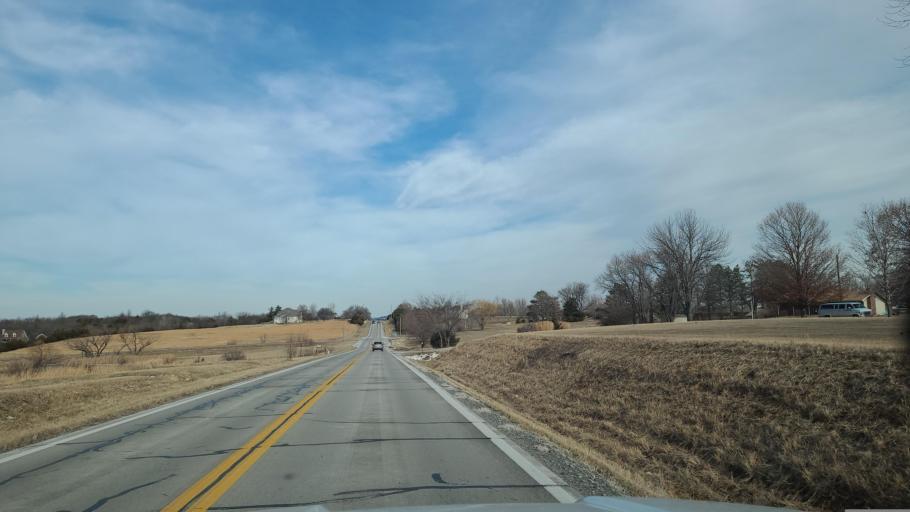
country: US
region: Kansas
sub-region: Douglas County
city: Baldwin City
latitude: 38.8233
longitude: -95.1864
